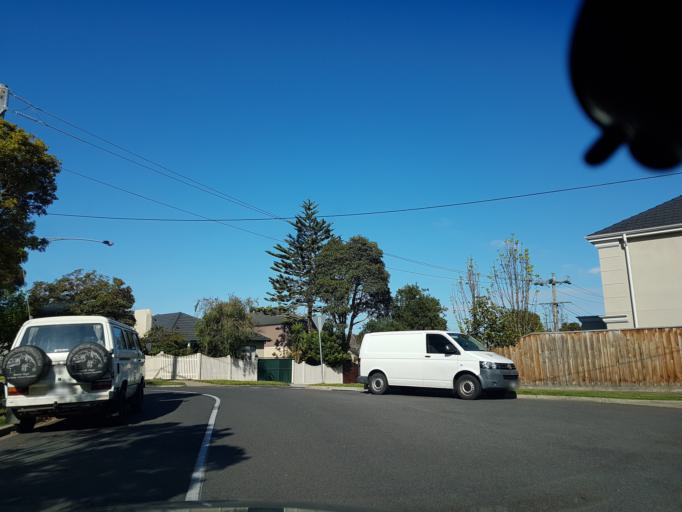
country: AU
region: Victoria
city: Ormond
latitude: -37.9078
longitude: 145.0277
